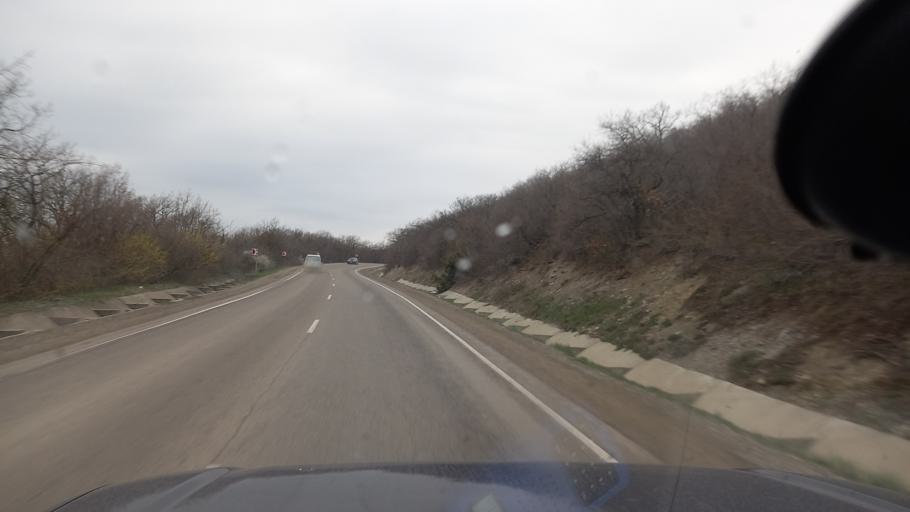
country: RU
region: Krasnodarskiy
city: Sukko
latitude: 44.8397
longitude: 37.4187
